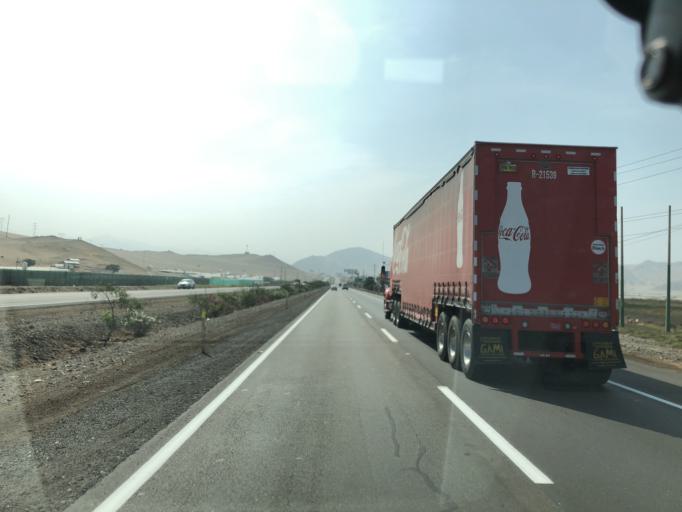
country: PE
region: Lima
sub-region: Provincia de Canete
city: Chilca
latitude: -12.5641
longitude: -76.7040
